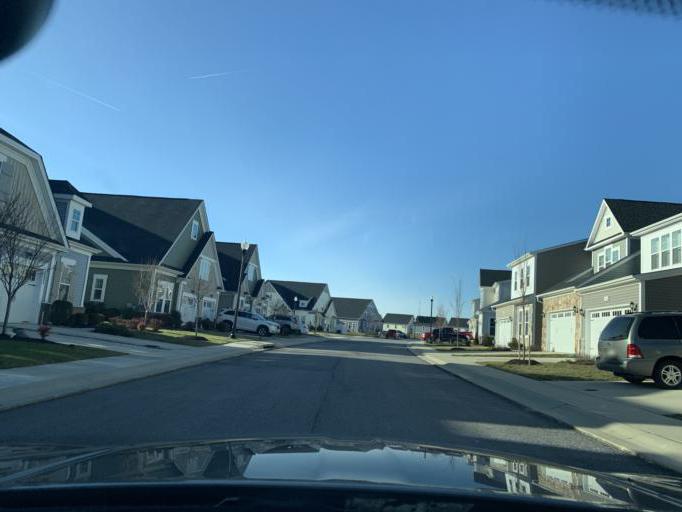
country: US
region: Maryland
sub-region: Anne Arundel County
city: Crofton
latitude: 39.0184
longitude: -76.7217
